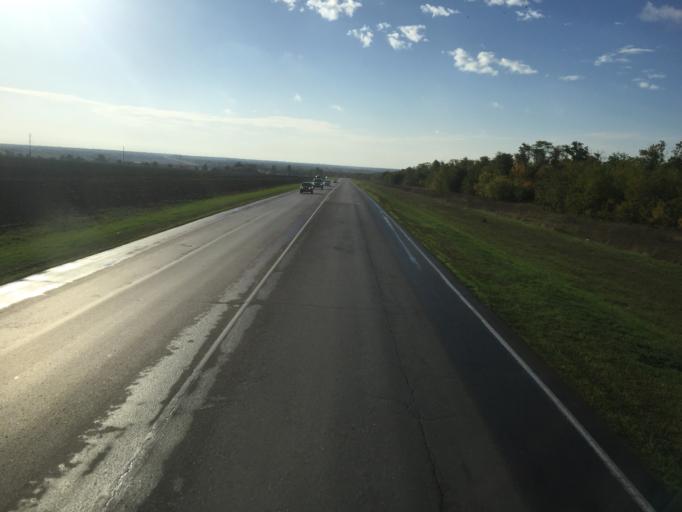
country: RU
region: Rostov
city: Mechetinskaya
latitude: 46.6802
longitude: 40.5230
